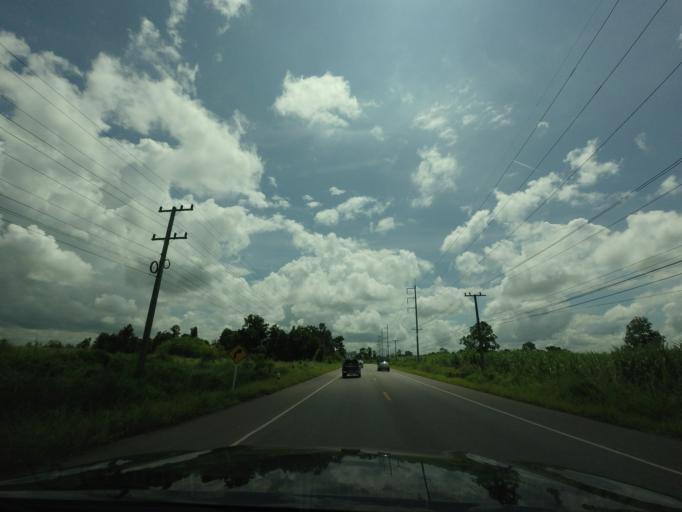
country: TH
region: Changwat Udon Thani
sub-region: Amphoe Ban Phue
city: Ban Phue
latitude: 17.6532
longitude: 102.5184
